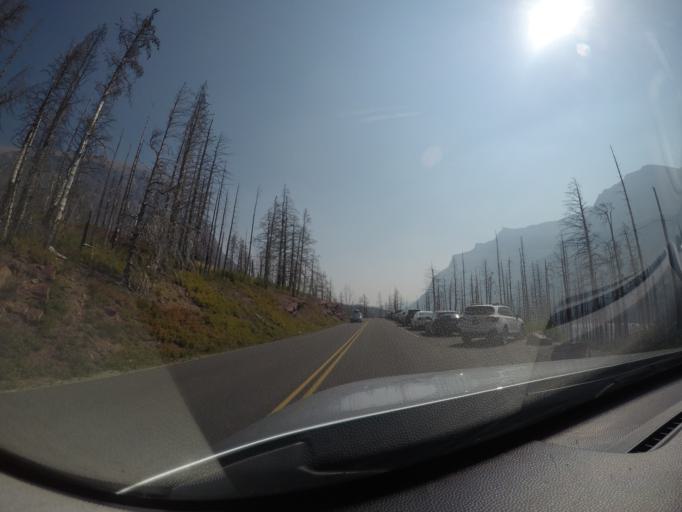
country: US
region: Montana
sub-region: Glacier County
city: Browning
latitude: 48.6758
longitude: -113.6001
